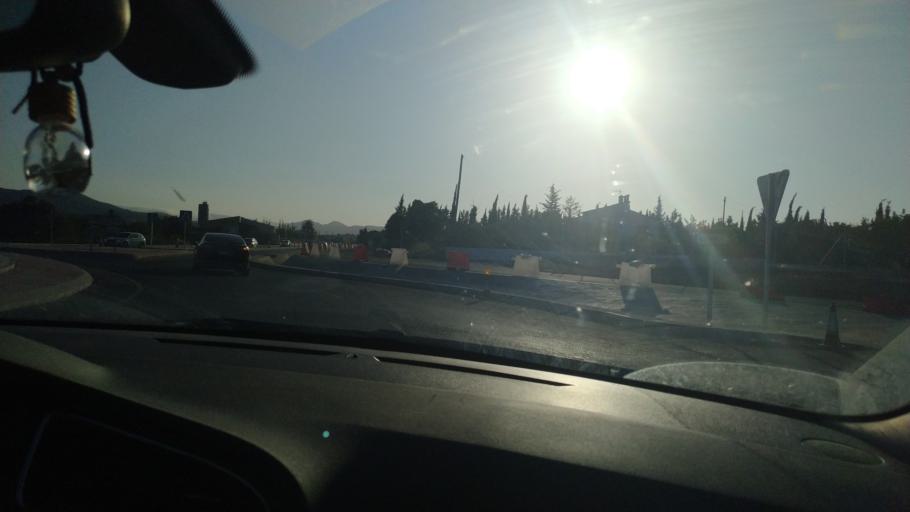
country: ES
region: Valencia
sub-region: Provincia de Alicante
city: Javea
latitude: 38.7756
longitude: 0.1408
